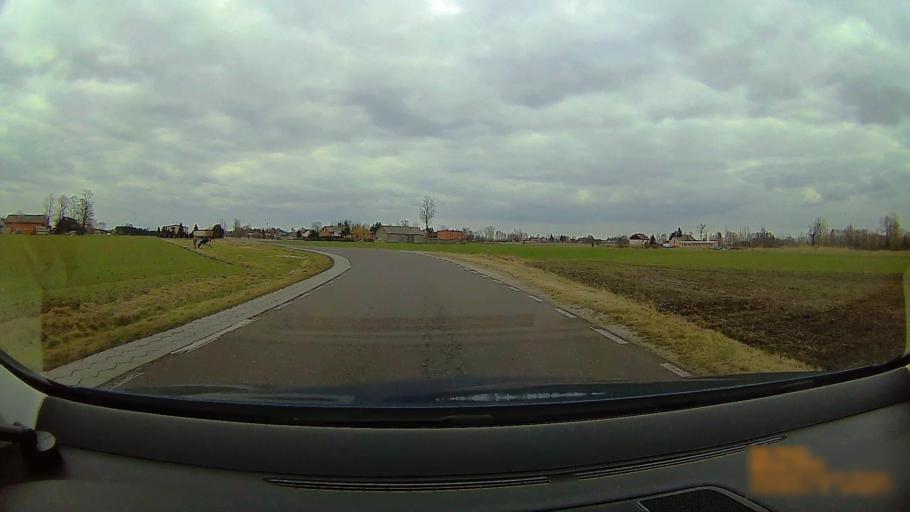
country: PL
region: Greater Poland Voivodeship
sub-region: Powiat koninski
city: Rzgow Pierwszy
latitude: 52.1068
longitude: 18.0827
